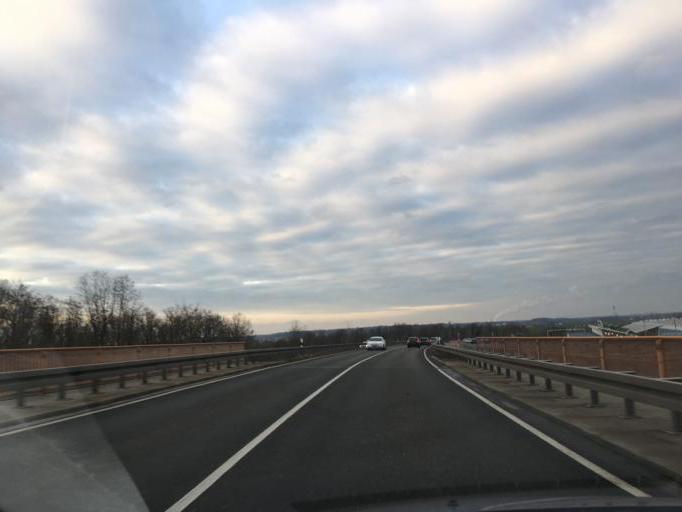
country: DE
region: Thuringia
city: Altenburg
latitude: 51.0110
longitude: 12.4553
